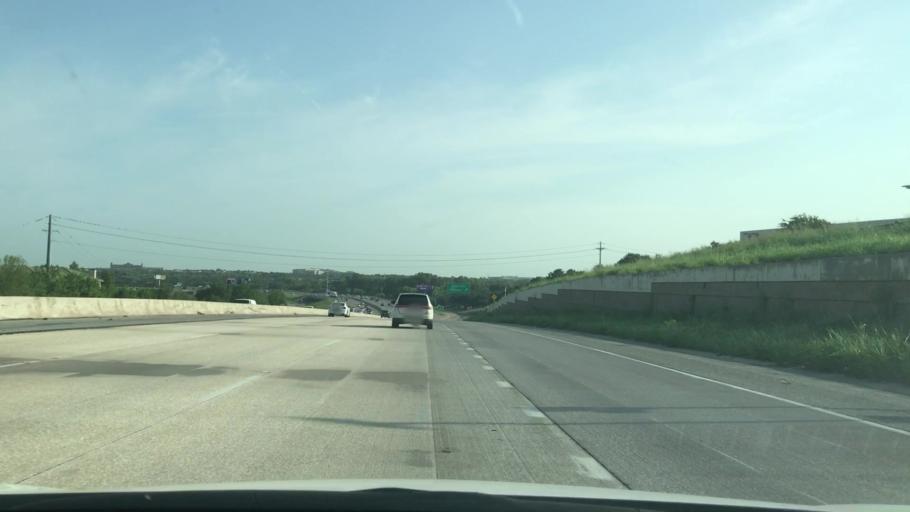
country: US
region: Texas
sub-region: Tarrant County
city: Euless
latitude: 32.7995
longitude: -97.0550
